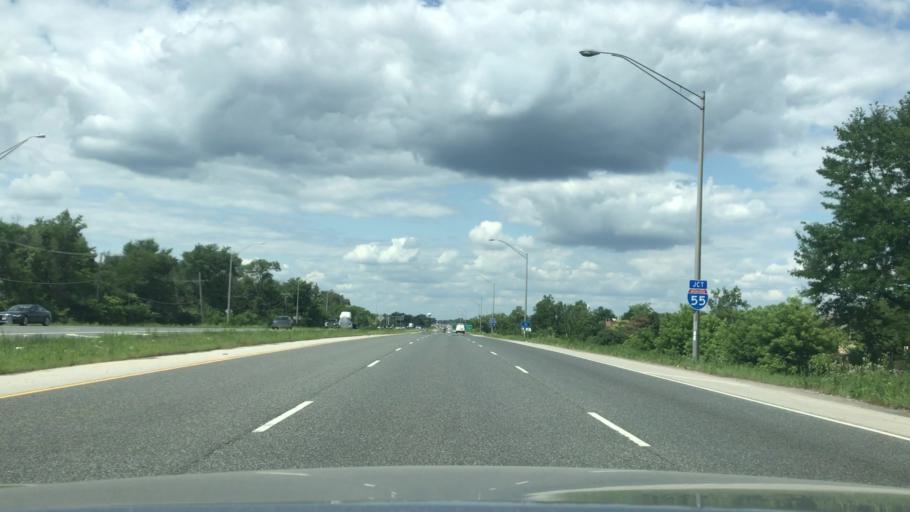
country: US
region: Illinois
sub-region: DuPage County
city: Burr Ridge
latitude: 41.7349
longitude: -87.9440
